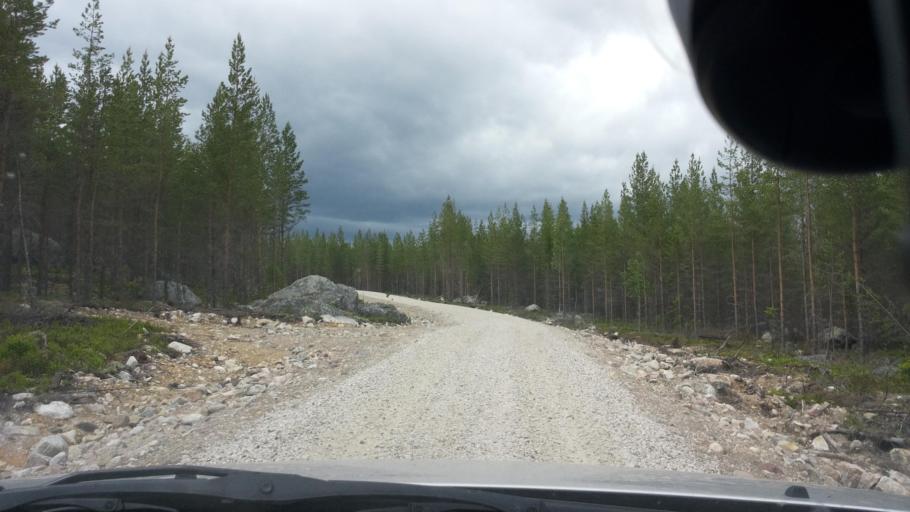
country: SE
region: Gaevleborg
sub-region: Ovanakers Kommun
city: Edsbyn
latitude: 61.4641
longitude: 15.2912
